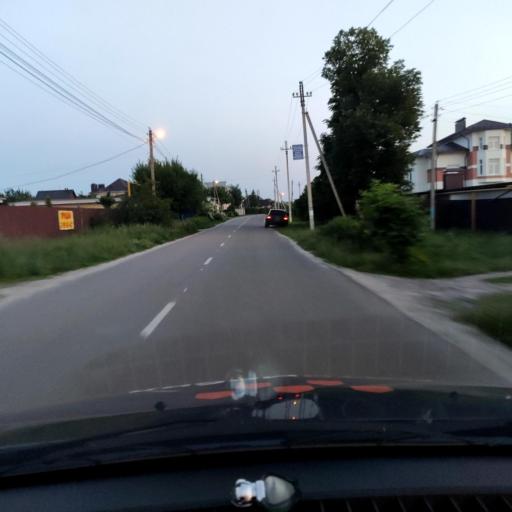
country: RU
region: Voronezj
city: Ramon'
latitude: 51.8155
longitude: 39.2642
